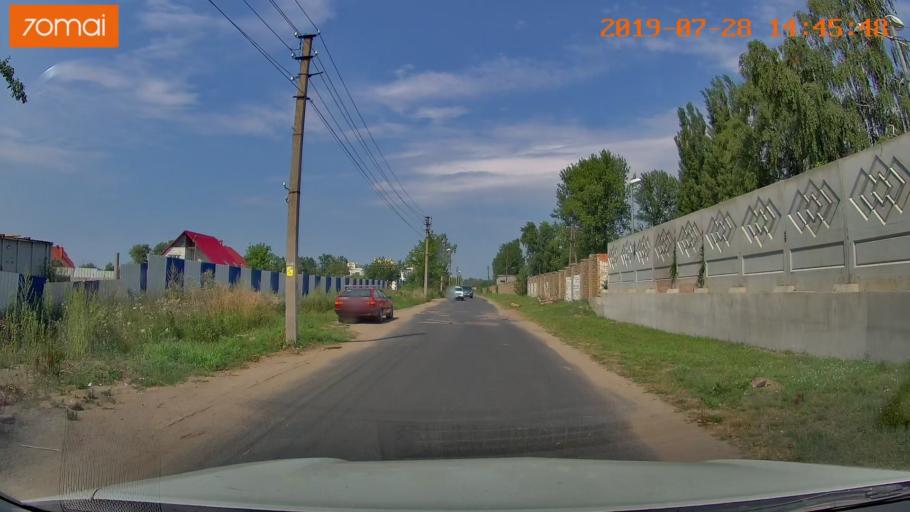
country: RU
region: Kaliningrad
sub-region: Gorod Kaliningrad
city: Yantarnyy
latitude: 54.8728
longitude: 19.9397
